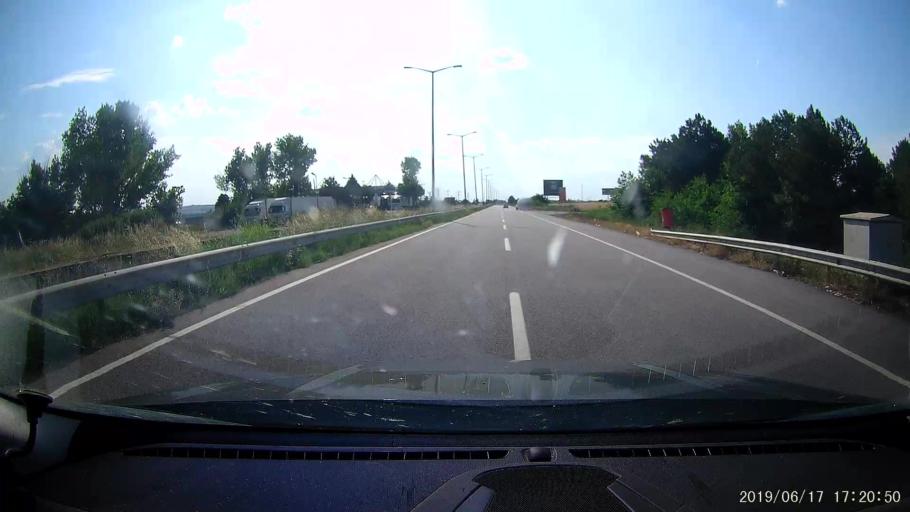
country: GR
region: East Macedonia and Thrace
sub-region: Nomos Evrou
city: Rizia
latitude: 41.7033
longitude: 26.4064
